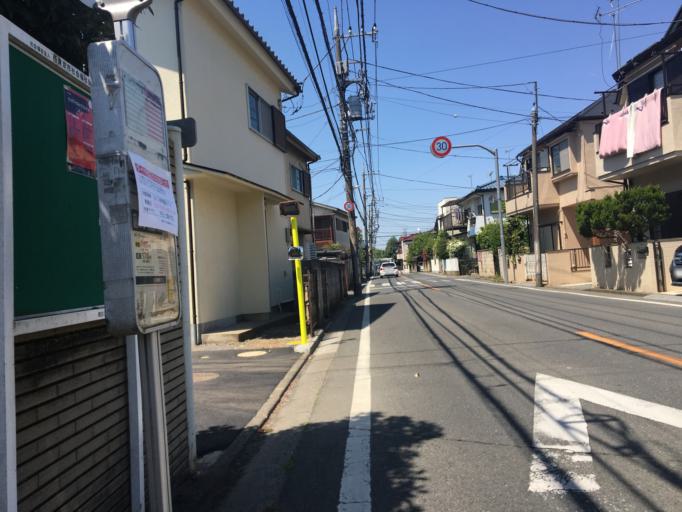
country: JP
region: Tokyo
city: Nishi-Tokyo-shi
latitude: 35.7187
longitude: 139.5267
